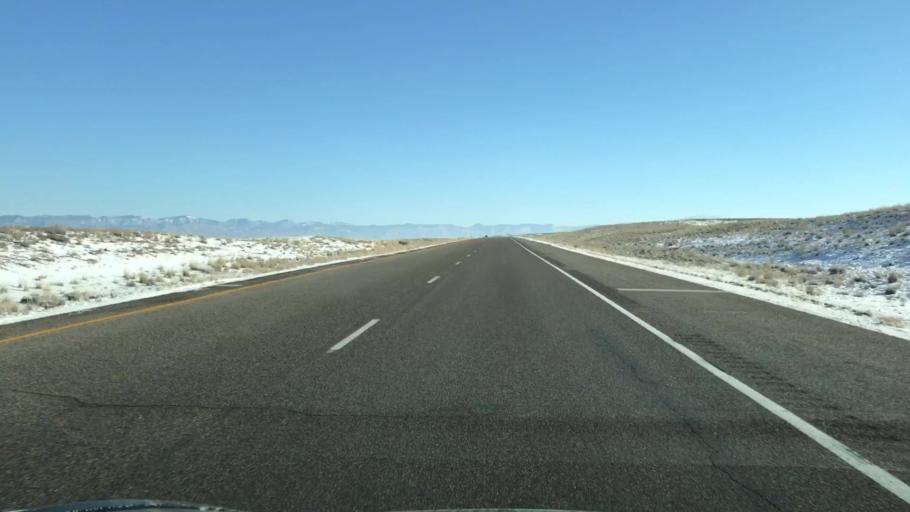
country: US
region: Colorado
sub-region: Mesa County
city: Loma
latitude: 39.2261
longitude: -108.9287
